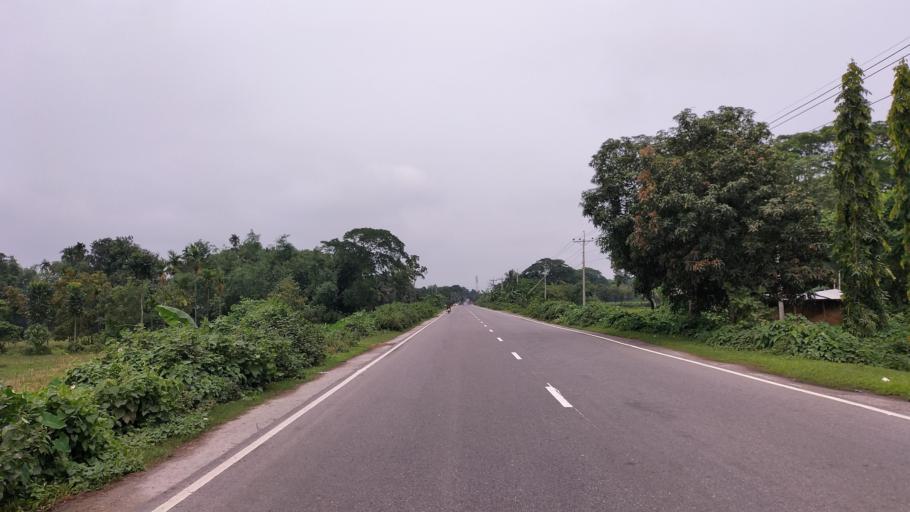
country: BD
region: Dhaka
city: Netrakona
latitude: 24.8507
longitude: 90.6331
